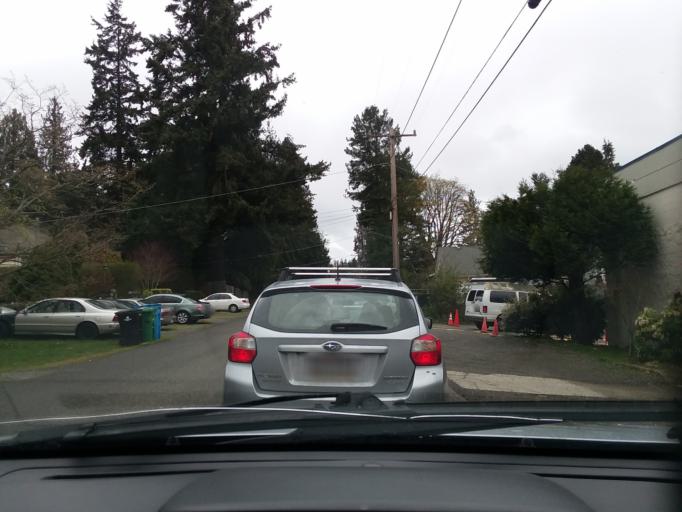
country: US
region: Washington
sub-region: King County
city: Shoreline
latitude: 47.7348
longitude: -122.3112
